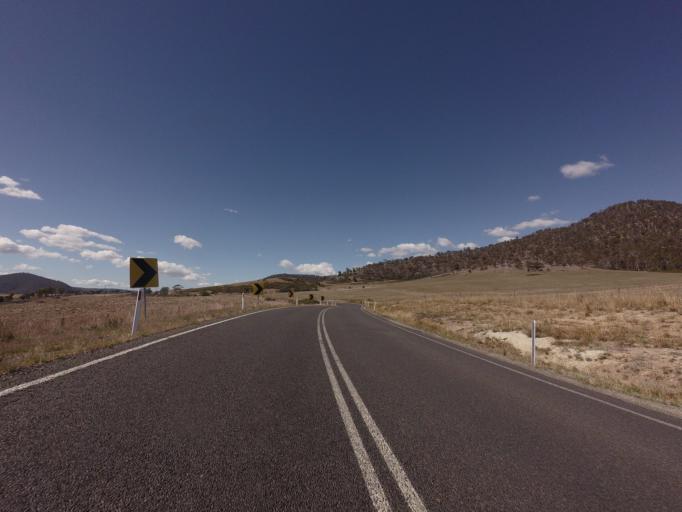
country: AU
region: Tasmania
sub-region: Break O'Day
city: St Helens
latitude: -41.6988
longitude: 147.8591
